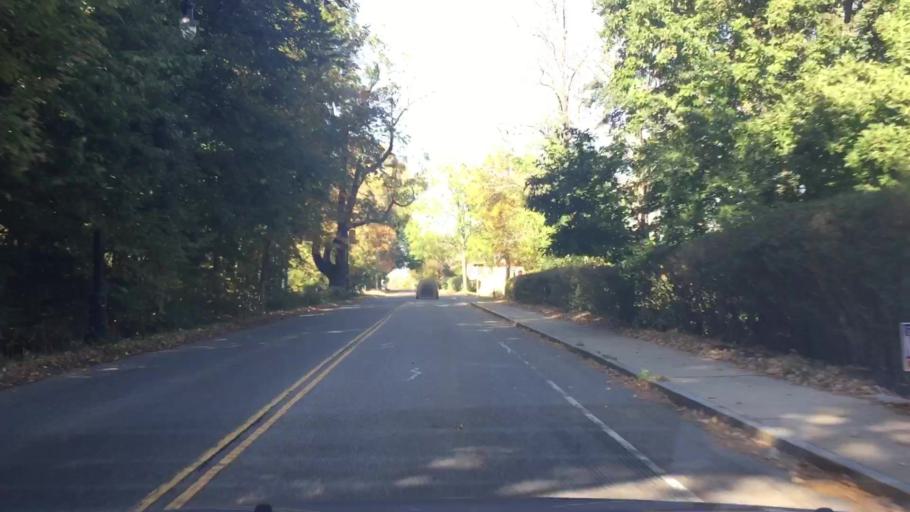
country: US
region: Massachusetts
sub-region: Essex County
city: North Andover
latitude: 42.6878
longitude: -71.1174
